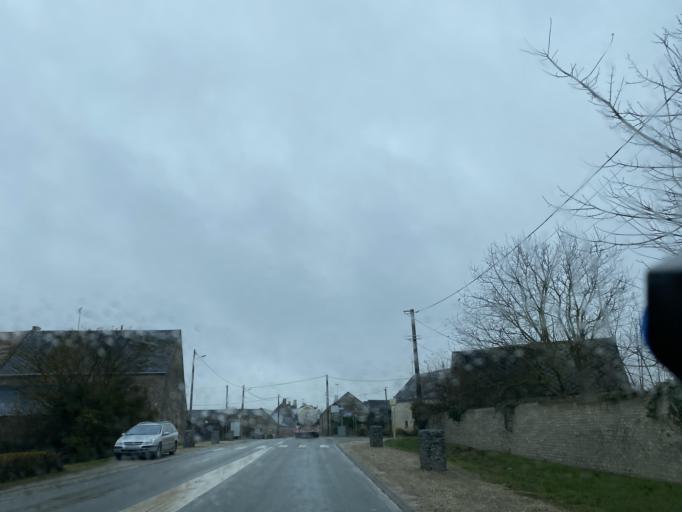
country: FR
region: Centre
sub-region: Departement d'Eure-et-Loir
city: Janville
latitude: 48.2059
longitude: 1.8226
